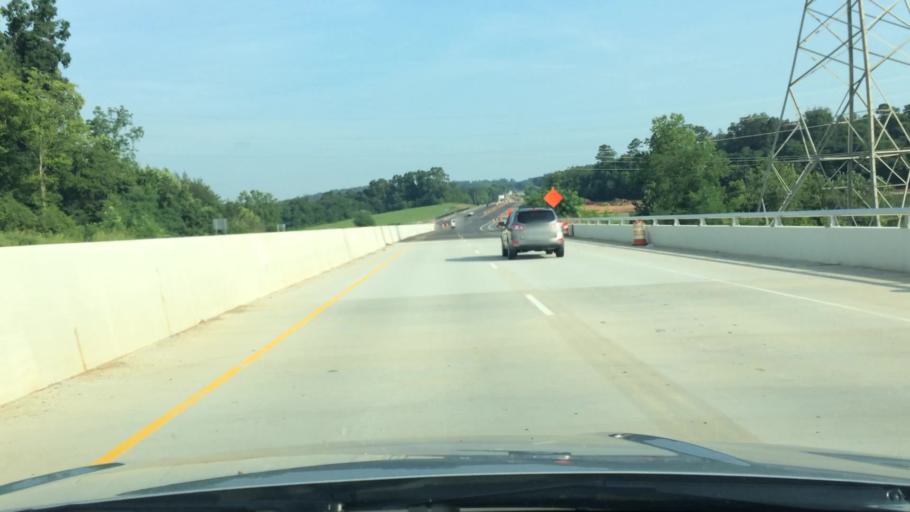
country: US
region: Tennessee
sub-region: Loudon County
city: Lenoir City
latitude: 35.7894
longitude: -84.2497
